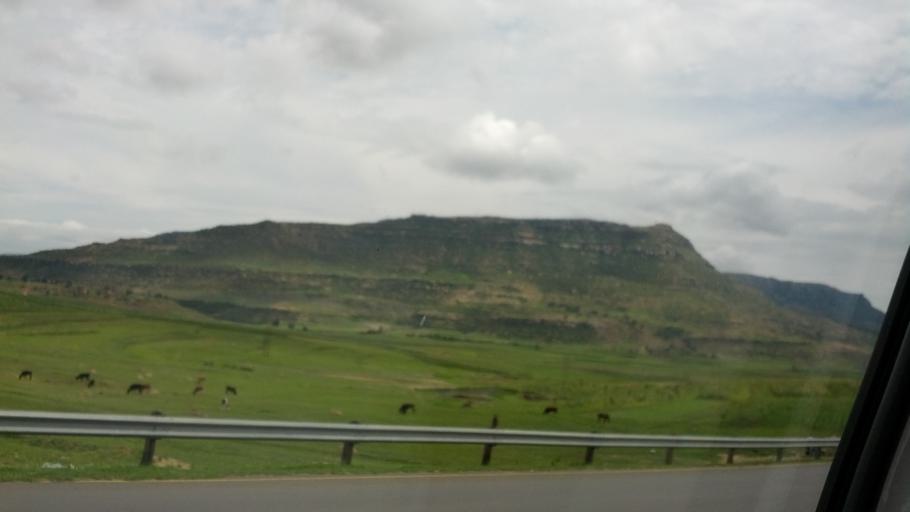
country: LS
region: Maseru
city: Maseru
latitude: -29.5407
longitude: 27.5096
